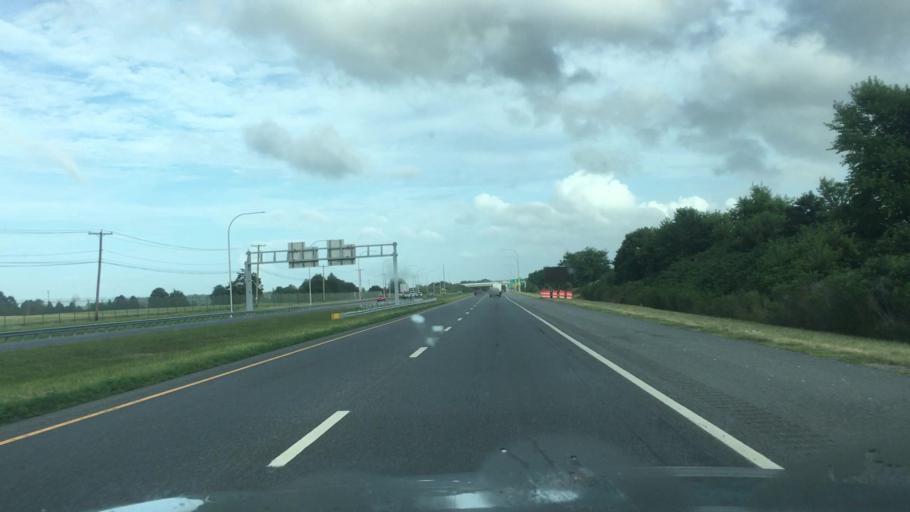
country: US
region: Delaware
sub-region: Kent County
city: Dover Base Housing
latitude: 39.1104
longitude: -75.4618
